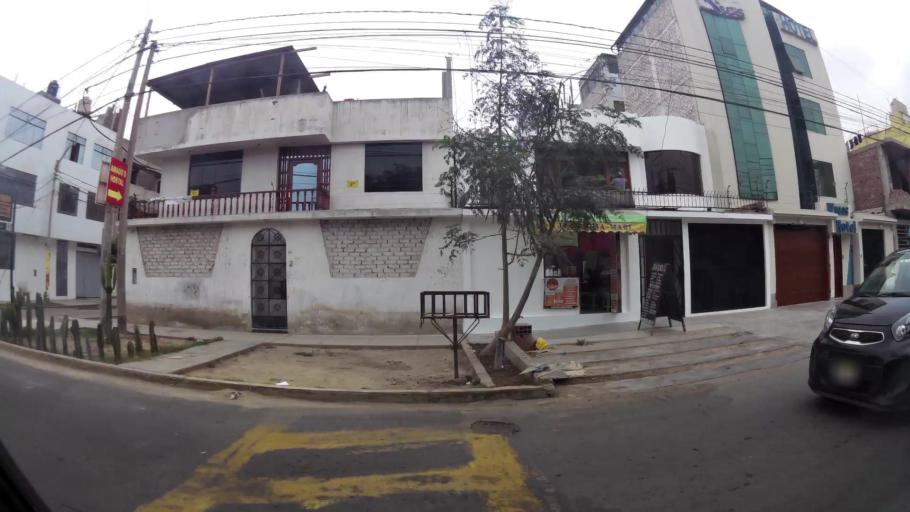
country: PE
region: La Libertad
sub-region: Provincia de Trujillo
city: Trujillo
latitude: -8.1159
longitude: -79.0437
